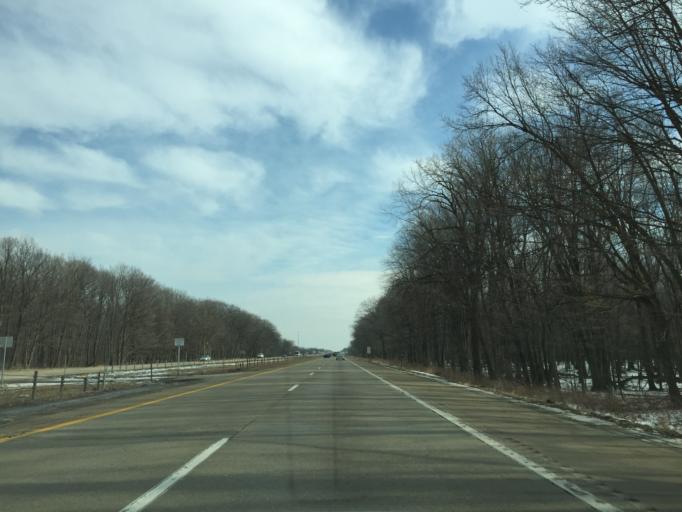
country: US
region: Michigan
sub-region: Ionia County
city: Ionia
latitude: 42.8790
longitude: -85.0630
